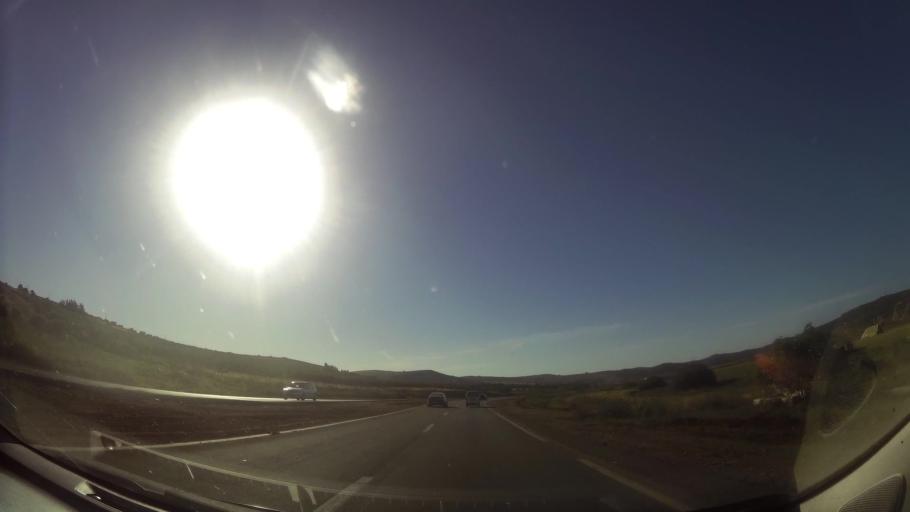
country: MA
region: Oriental
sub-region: Berkane-Taourirt
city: Madagh
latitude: 35.0367
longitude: -2.2062
